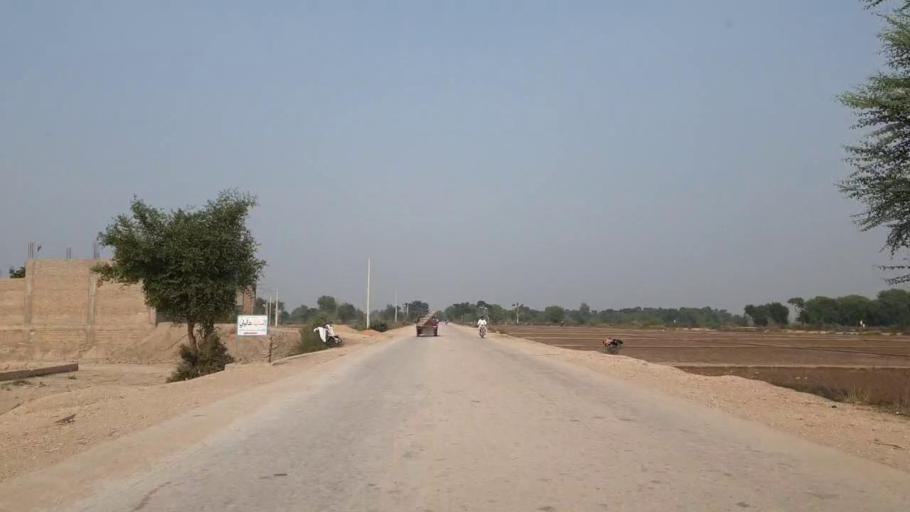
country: PK
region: Sindh
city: Bhan
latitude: 26.5699
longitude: 67.7260
